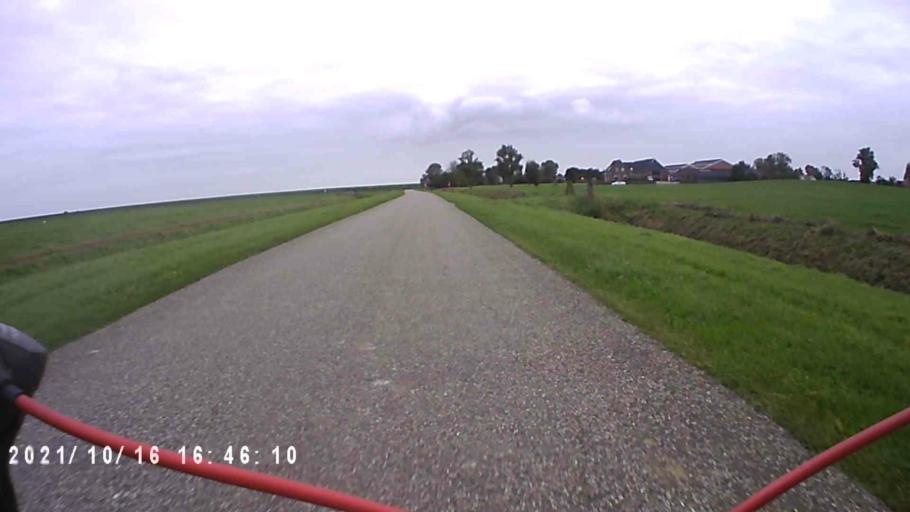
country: NL
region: Friesland
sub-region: Gemeente Dongeradeel
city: Anjum
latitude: 53.3626
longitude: 6.1435
